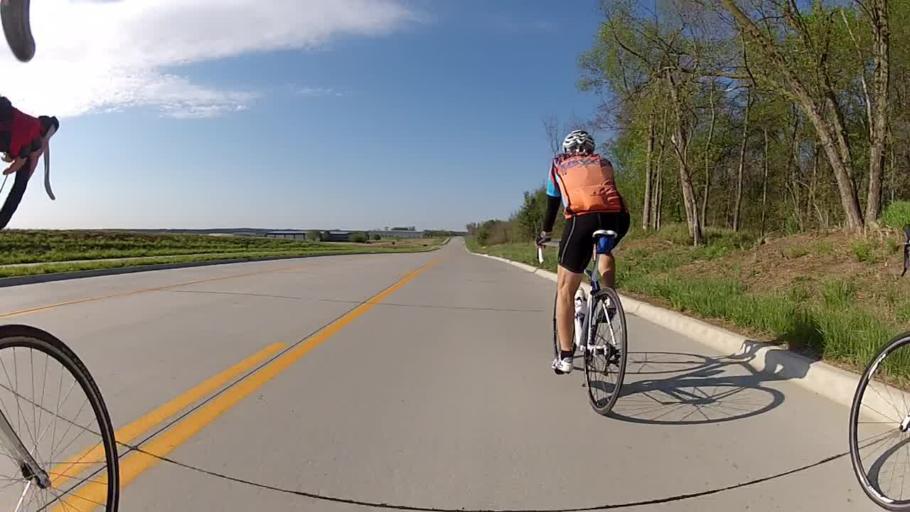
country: US
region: Kansas
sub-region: Riley County
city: Ogden
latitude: 39.1467
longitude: -96.6819
